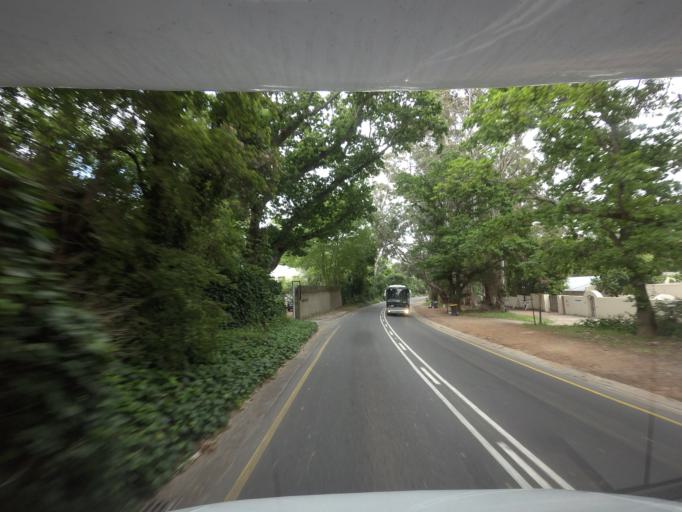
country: ZA
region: Western Cape
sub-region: City of Cape Town
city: Constantia
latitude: -34.0138
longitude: 18.3885
